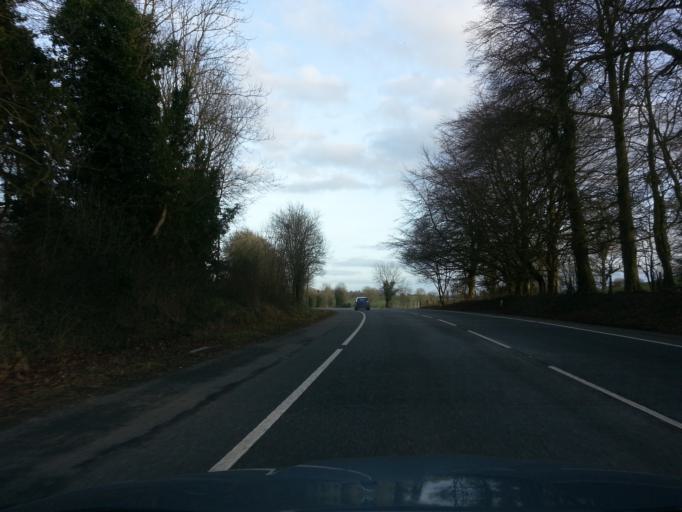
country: GB
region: Northern Ireland
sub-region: Fermanagh District
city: Enniskillen
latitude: 54.3196
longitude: -7.5917
